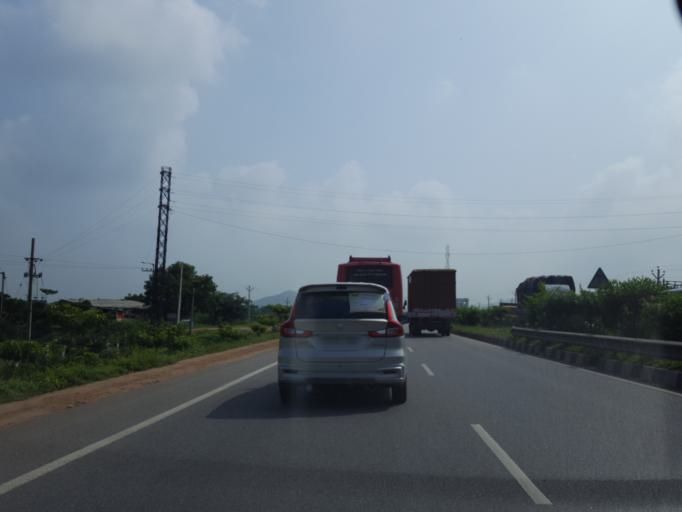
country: IN
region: Telangana
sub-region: Rangareddi
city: Ghatkesar
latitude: 17.2795
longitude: 78.7912
